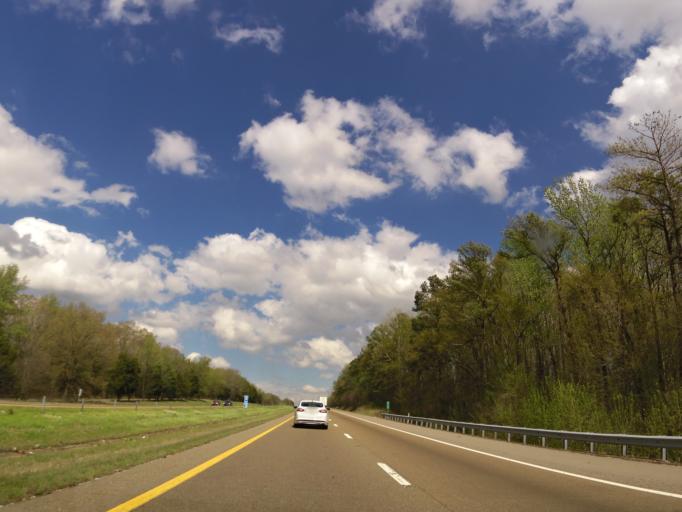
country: US
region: Tennessee
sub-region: Crockett County
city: Bells
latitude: 35.6193
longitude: -88.9931
